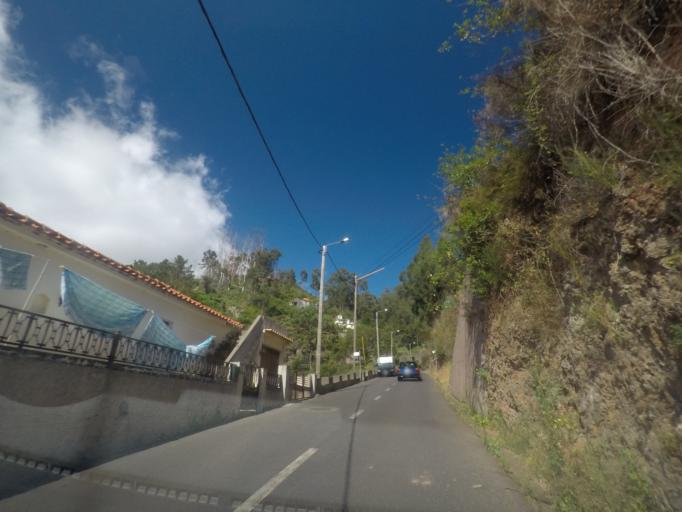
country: PT
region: Madeira
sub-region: Ribeira Brava
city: Campanario
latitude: 32.6905
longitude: -17.0315
